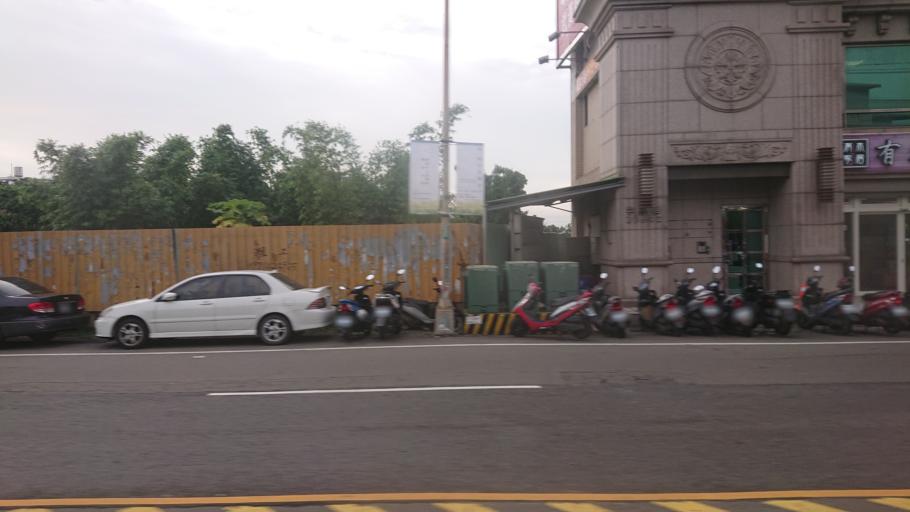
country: TW
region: Taiwan
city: Daxi
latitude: 24.8723
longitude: 121.2291
